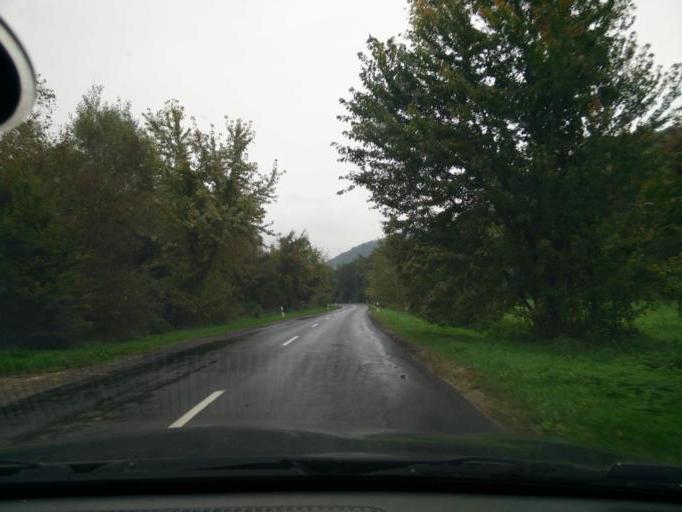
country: HU
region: Komarom-Esztergom
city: Tatabanya
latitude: 47.5700
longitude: 18.4507
